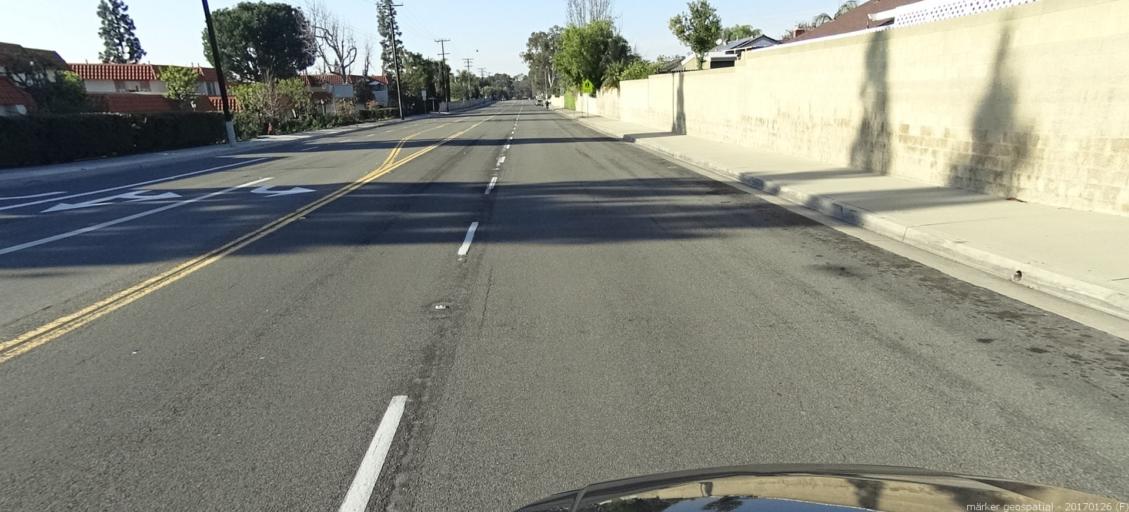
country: US
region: California
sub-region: Orange County
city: Lake Forest
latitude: 33.6329
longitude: -117.6859
